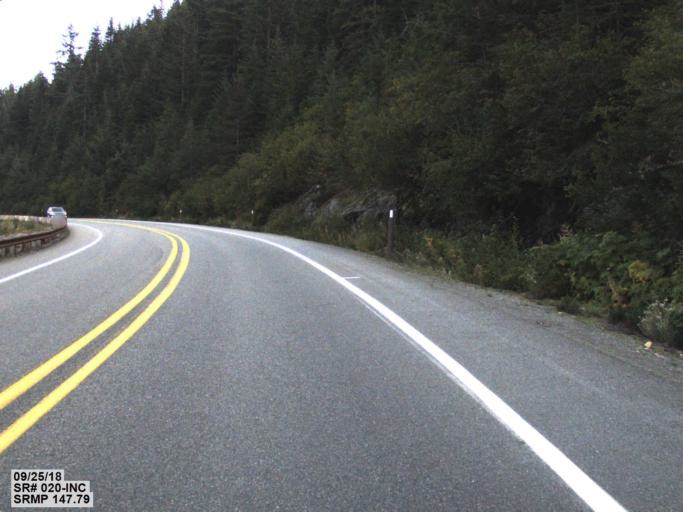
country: US
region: Washington
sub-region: Snohomish County
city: Darrington
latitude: 48.6309
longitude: -120.8457
